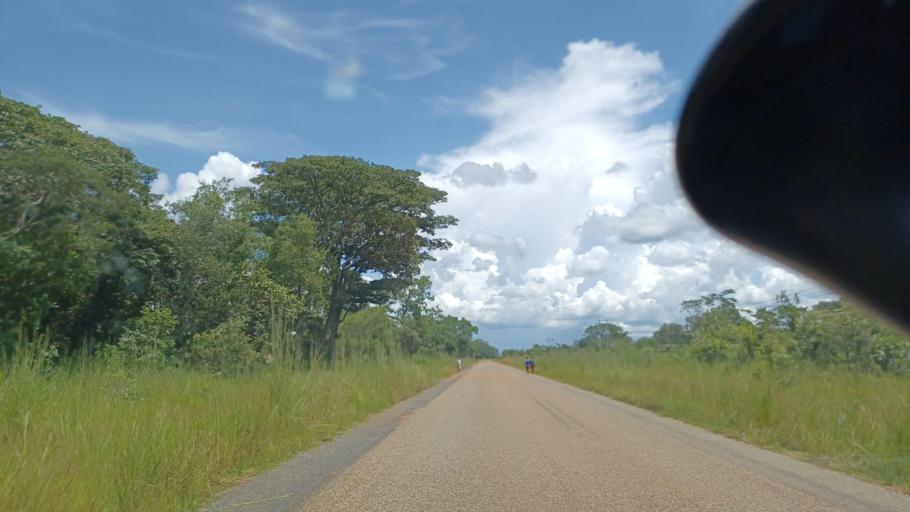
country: ZM
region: North-Western
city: Solwezi
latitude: -12.6032
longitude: 26.1257
